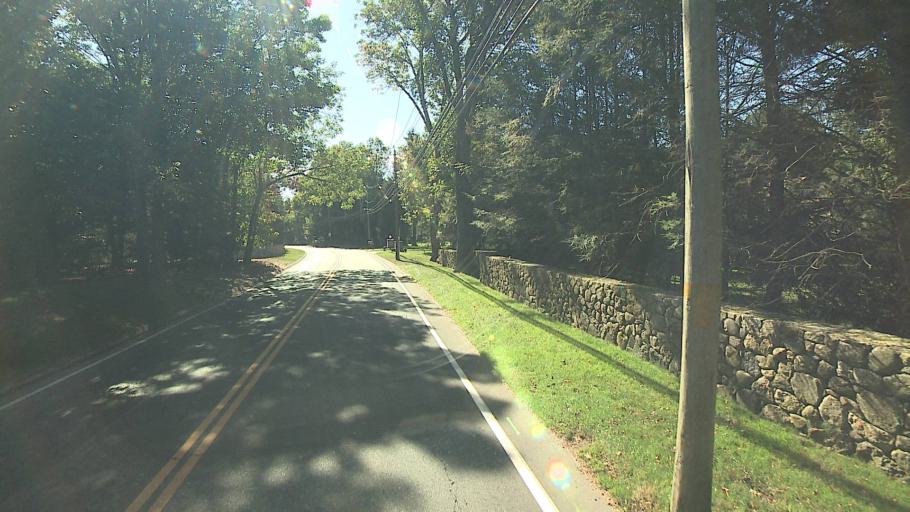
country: US
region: Connecticut
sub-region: Fairfield County
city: Darien
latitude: 41.0952
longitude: -73.4788
